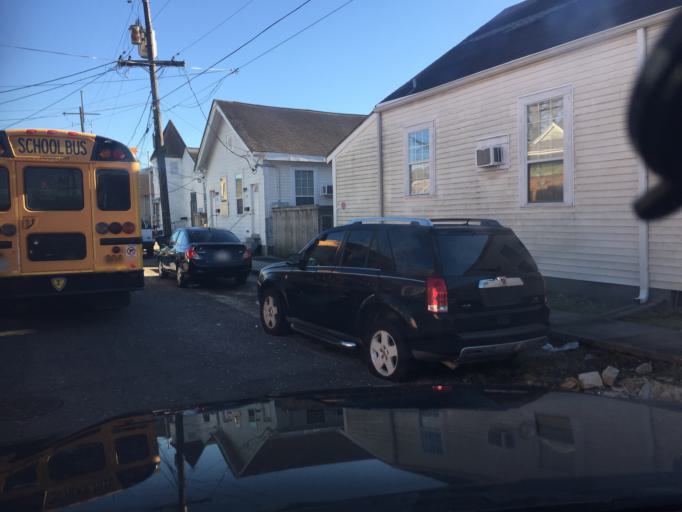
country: US
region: Louisiana
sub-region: Orleans Parish
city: New Orleans
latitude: 29.9778
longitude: -90.0695
